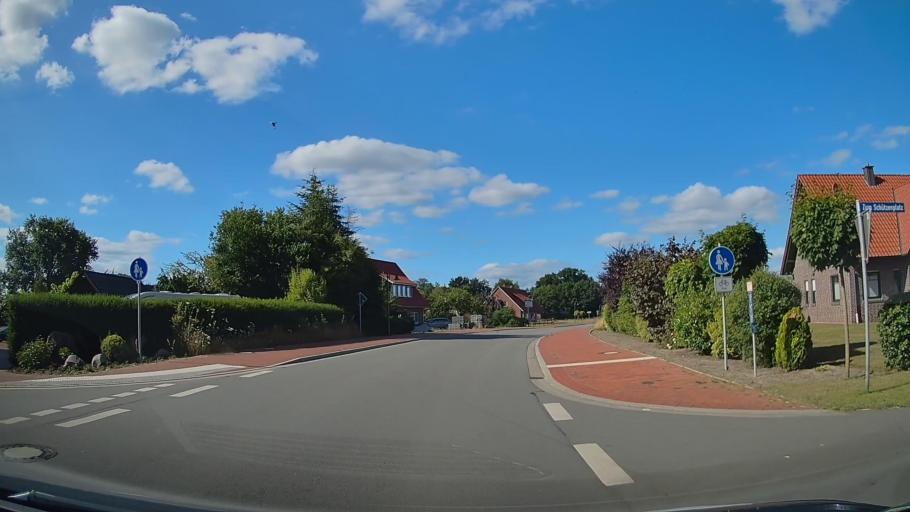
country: DE
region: Lower Saxony
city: Loningen
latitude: 52.7147
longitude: 7.7483
